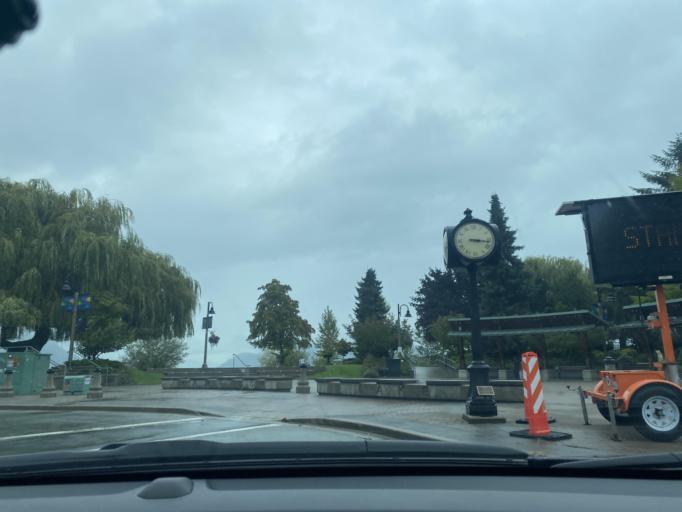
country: CA
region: British Columbia
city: Agassiz
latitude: 49.3032
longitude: -121.7853
